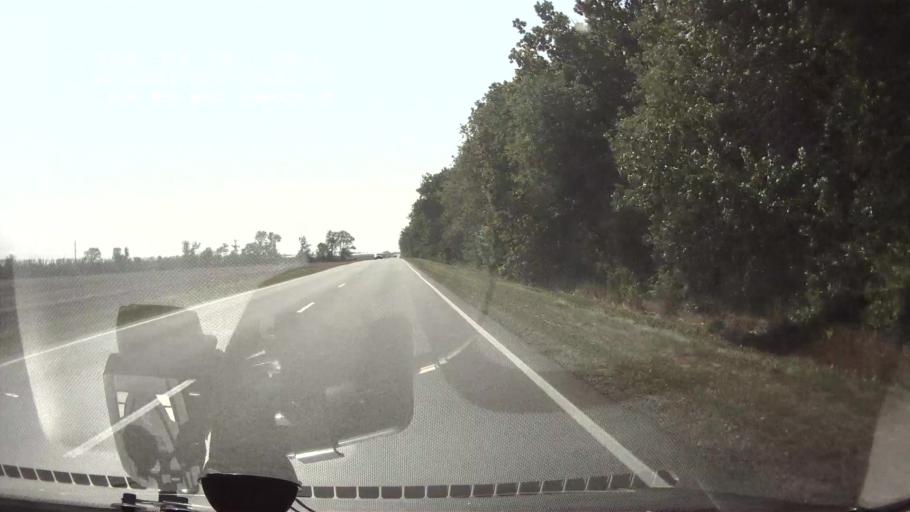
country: RU
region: Krasnodarskiy
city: Kavkazskaya
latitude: 45.5002
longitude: 40.6805
